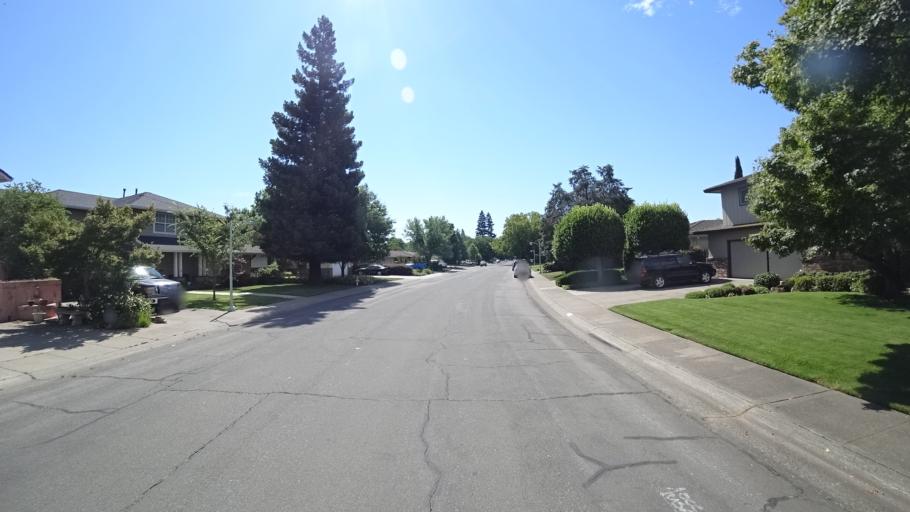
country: US
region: California
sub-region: Sacramento County
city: Sacramento
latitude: 38.5848
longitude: -121.4465
